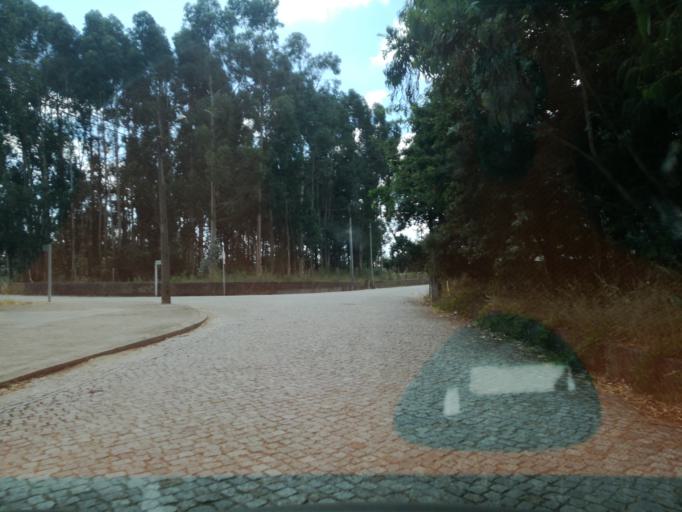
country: PT
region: Porto
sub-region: Maia
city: Nogueira
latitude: 41.2438
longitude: -8.5942
